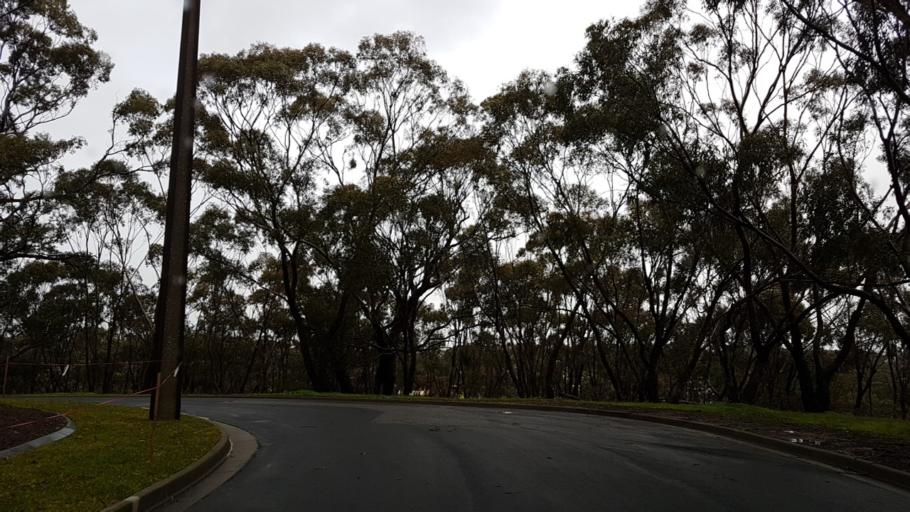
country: AU
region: South Australia
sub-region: Onkaparinga
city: Bedford Park
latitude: -35.0449
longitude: 138.5778
